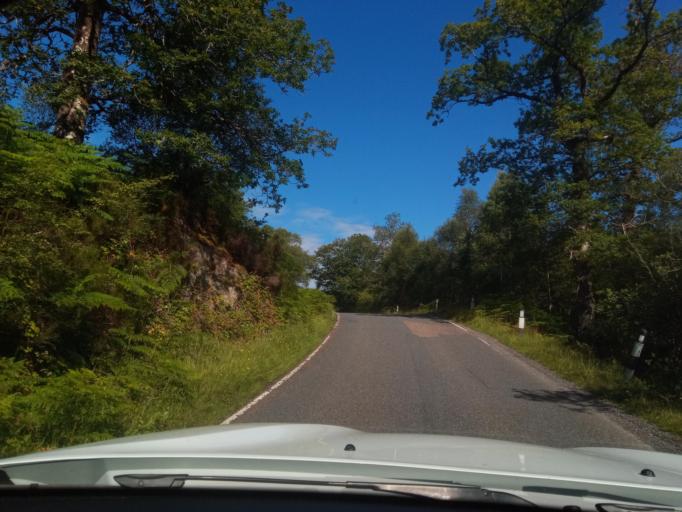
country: GB
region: Scotland
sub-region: Argyll and Bute
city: Isle Of Mull
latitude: 56.6974
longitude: -5.6858
